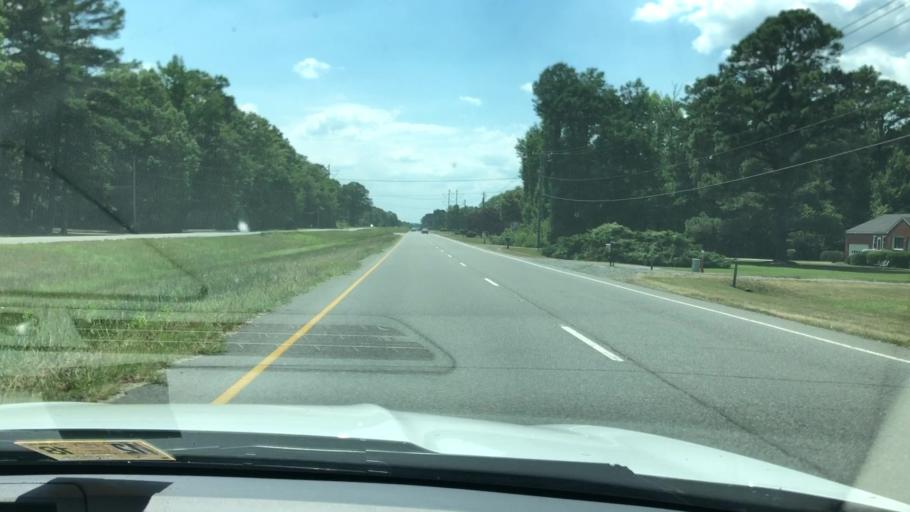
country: US
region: Virginia
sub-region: King William County
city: West Point
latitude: 37.5461
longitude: -76.7419
